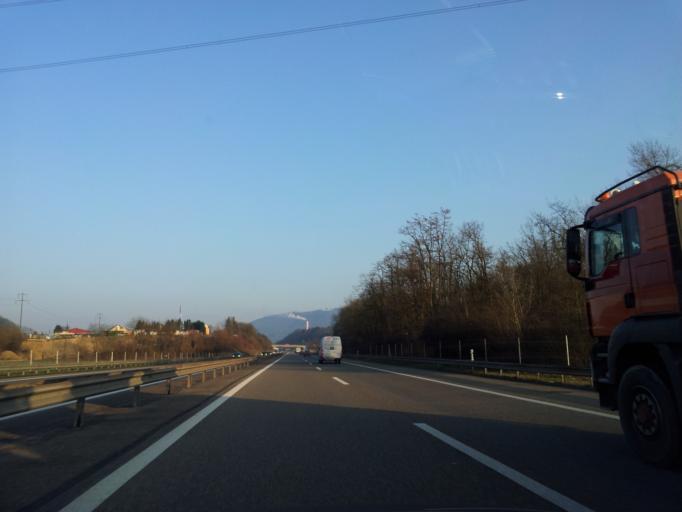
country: CH
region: Aargau
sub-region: Bezirk Laufenburg
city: Eiken
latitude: 47.5254
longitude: 8.0024
